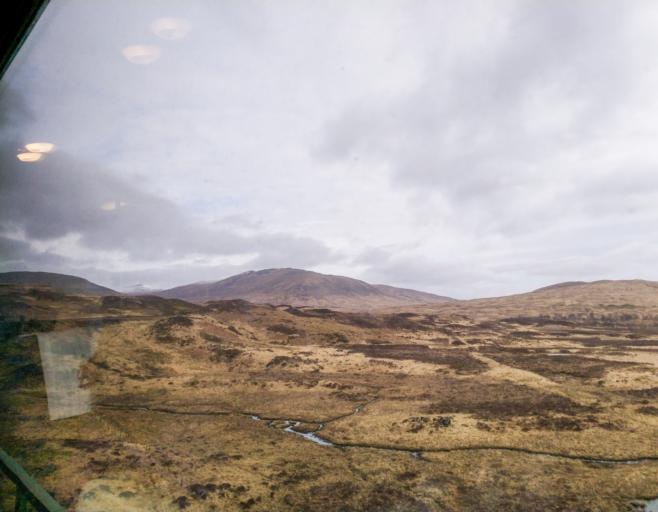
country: GB
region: Scotland
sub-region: Highland
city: Spean Bridge
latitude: 56.6893
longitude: -4.5767
